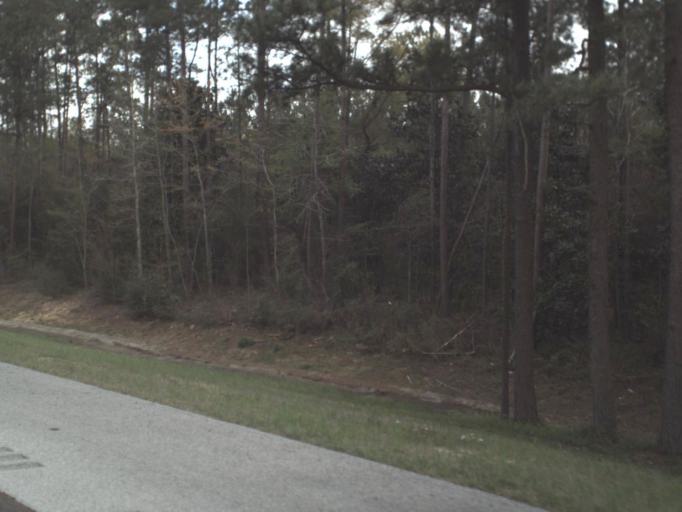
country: US
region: Florida
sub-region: Walton County
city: DeFuniak Springs
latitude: 30.6995
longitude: -86.1542
